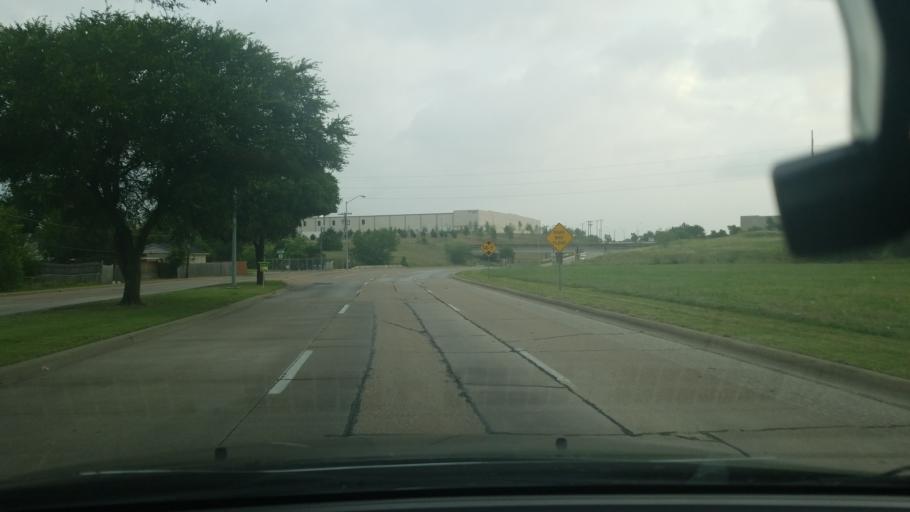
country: US
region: Texas
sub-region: Dallas County
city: Mesquite
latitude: 32.7719
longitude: -96.6289
